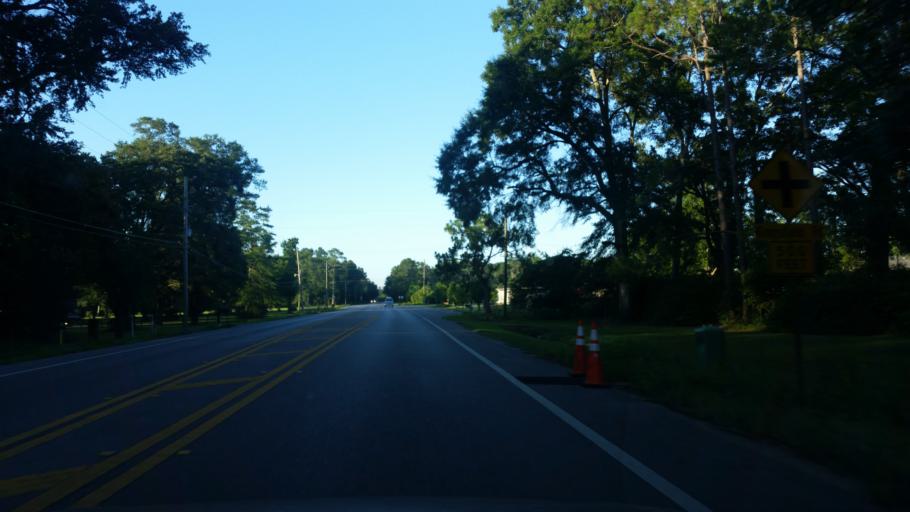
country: US
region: Florida
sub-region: Escambia County
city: Cantonment
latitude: 30.5803
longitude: -87.3495
